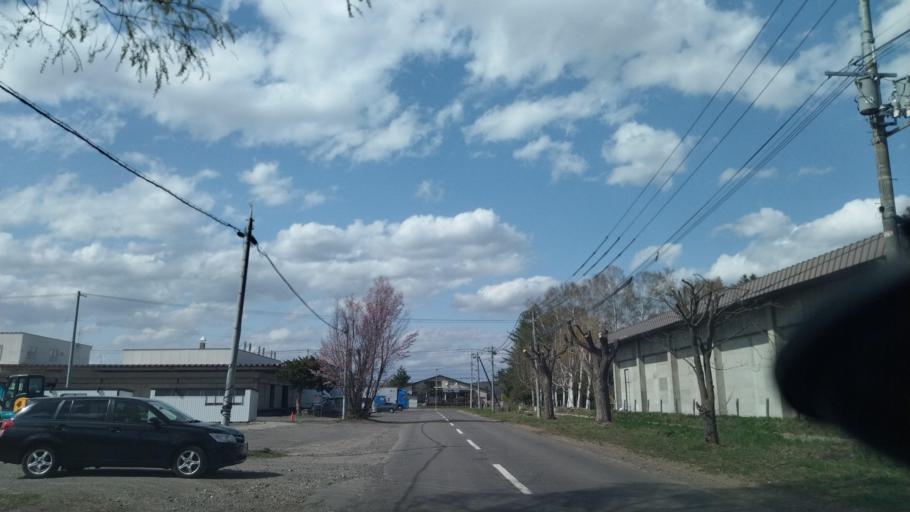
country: JP
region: Hokkaido
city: Obihiro
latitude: 42.9308
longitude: 143.1354
